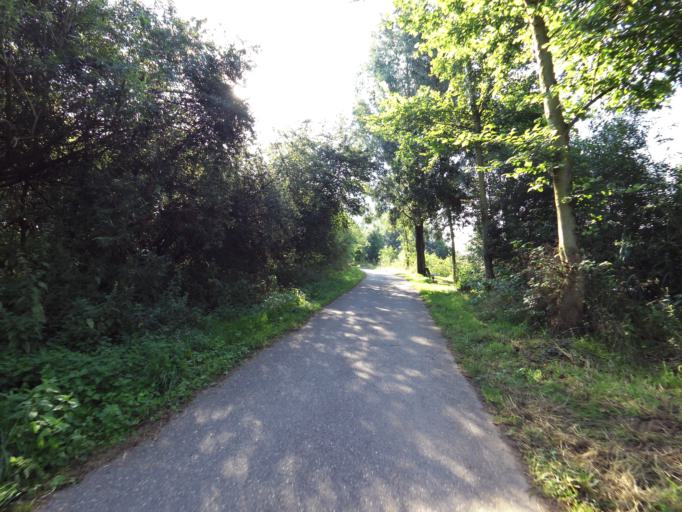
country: DE
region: North Rhine-Westphalia
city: Huckelhoven
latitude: 51.0489
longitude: 6.1937
